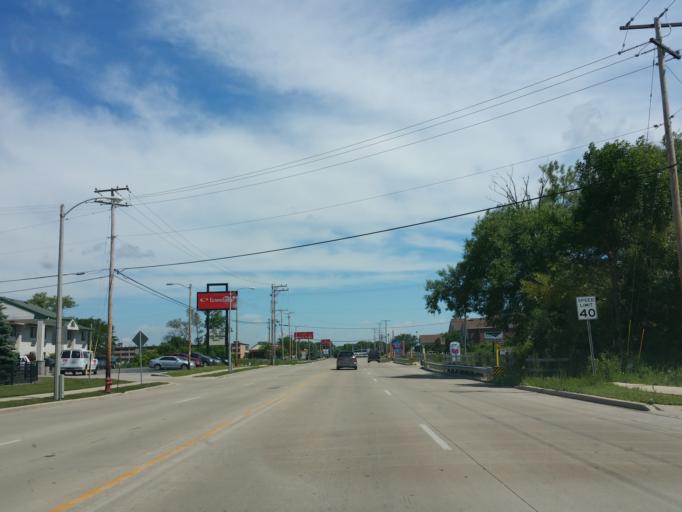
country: US
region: Wisconsin
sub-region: Milwaukee County
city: Greendale
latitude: 42.9255
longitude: -87.9304
